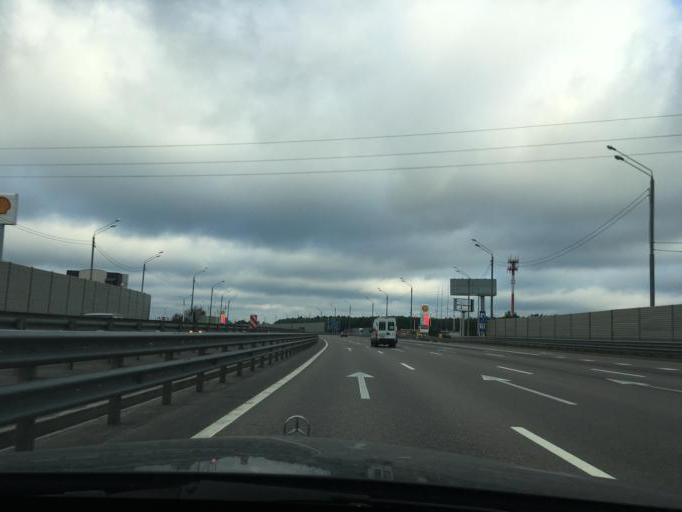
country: RU
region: Moskovskaya
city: Rozhdestveno
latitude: 55.8166
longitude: 37.0209
